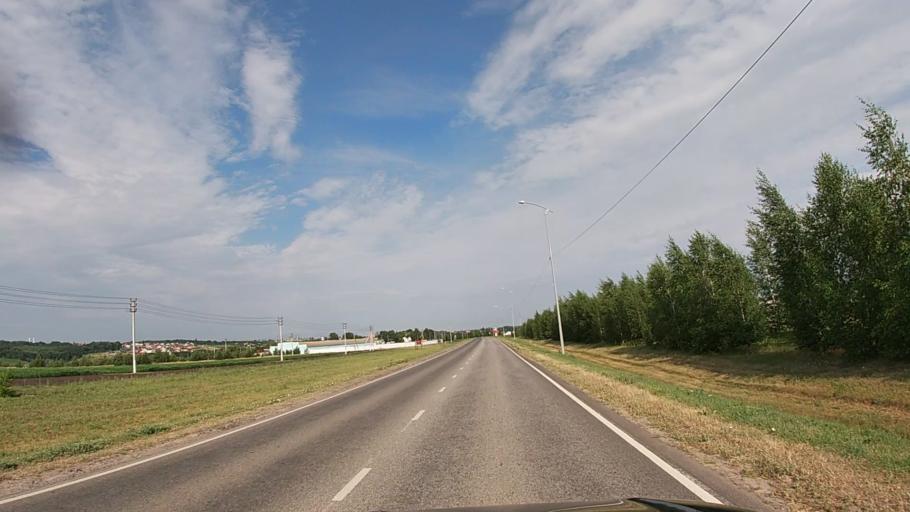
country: RU
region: Belgorod
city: Krasnaya Yaruga
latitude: 50.7978
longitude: 35.6845
